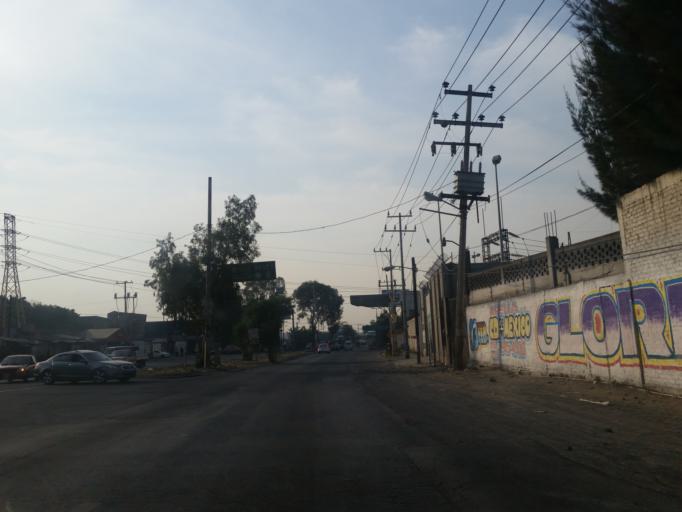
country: MX
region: Mexico
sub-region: La Paz
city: Emiliano Zapata
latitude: 19.3512
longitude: -98.9712
